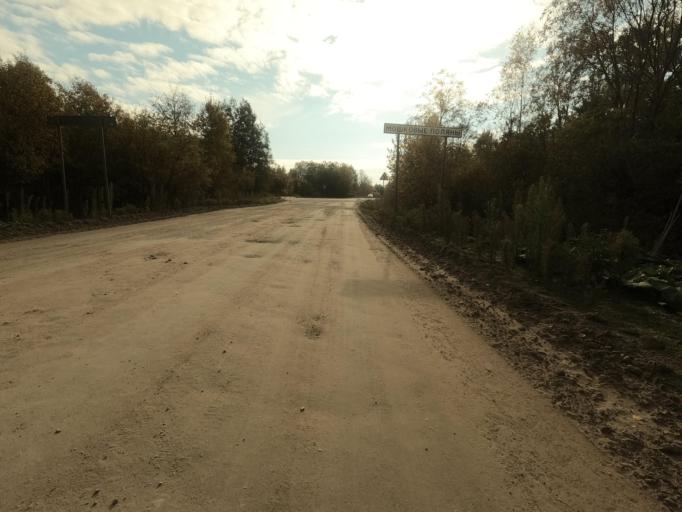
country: RU
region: Novgorod
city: Batetskiy
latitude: 58.8005
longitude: 30.6537
